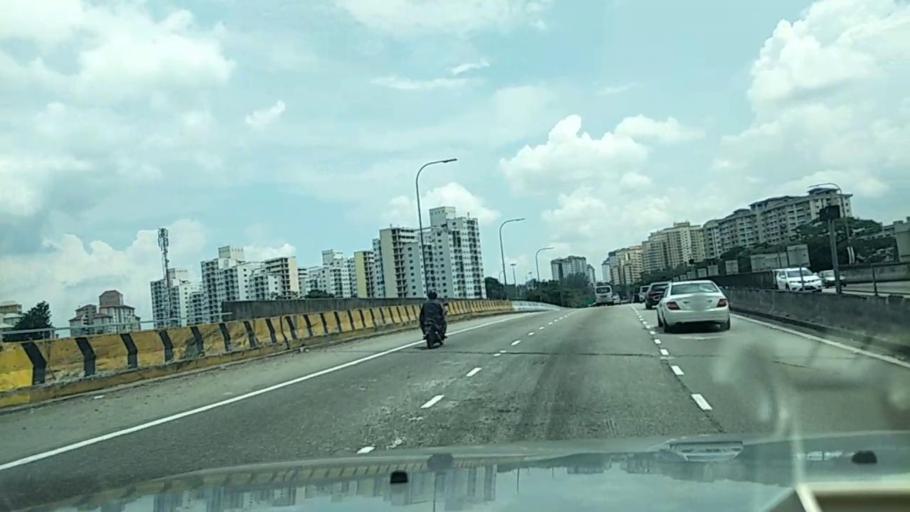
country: MY
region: Selangor
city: Kampong Baharu Balakong
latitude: 3.0670
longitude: 101.7089
